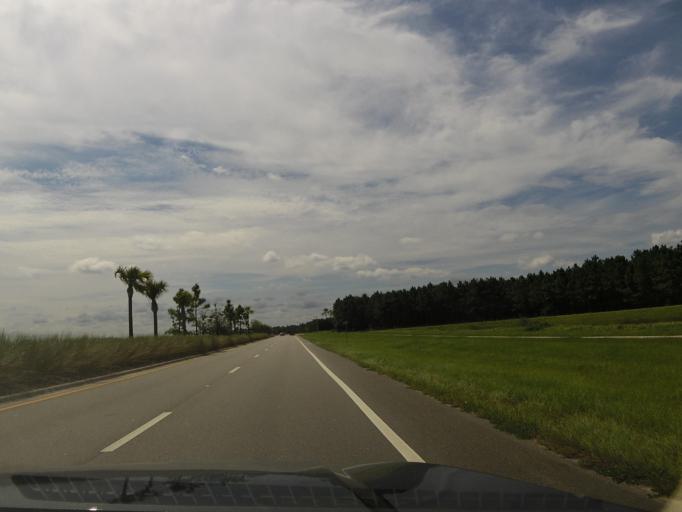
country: US
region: Florida
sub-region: Clay County
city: Green Cove Springs
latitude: 29.9958
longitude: -81.5098
